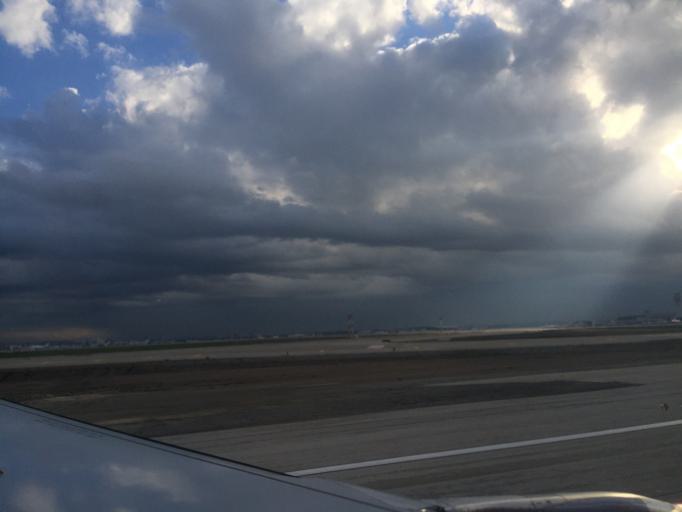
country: IL
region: Central District
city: Yehud
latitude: 32.0169
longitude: 34.8874
